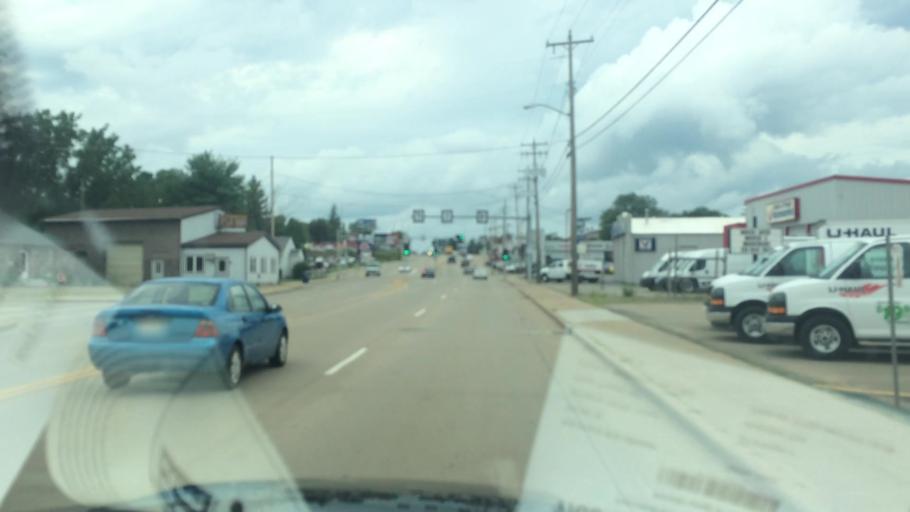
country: US
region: Wisconsin
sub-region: Marathon County
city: Schofield
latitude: 44.9296
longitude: -89.6142
